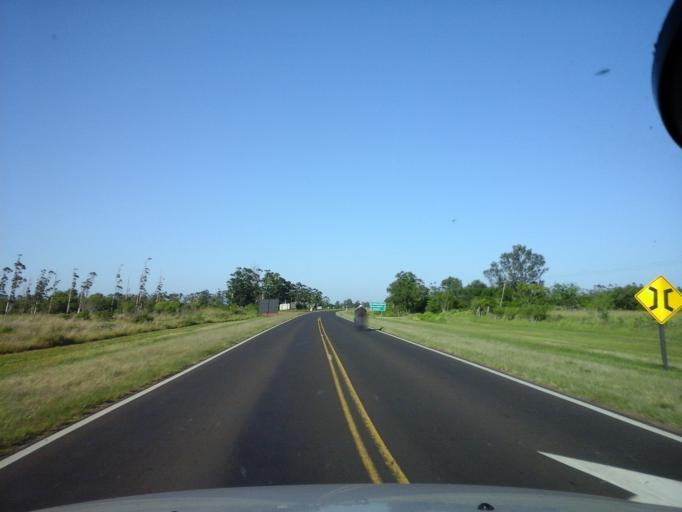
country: AR
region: Corrientes
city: Ita Ibate
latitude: -27.4404
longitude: -57.3531
